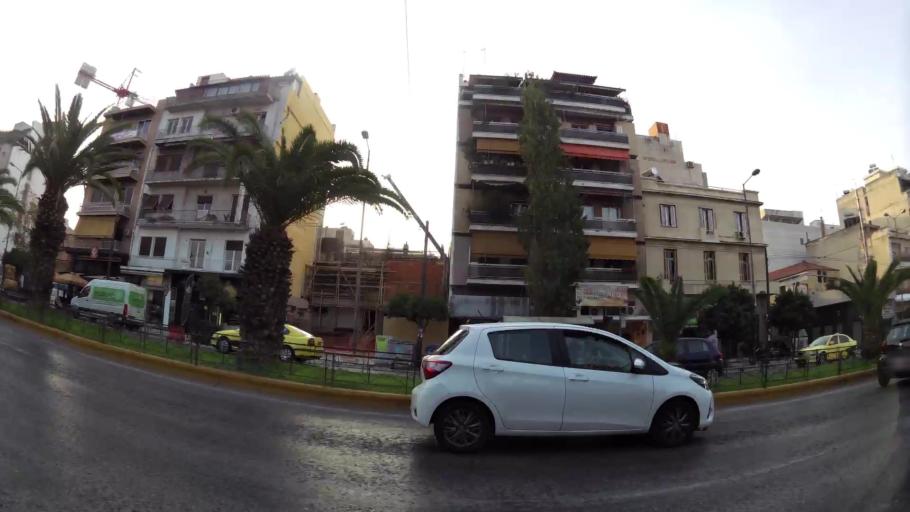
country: GR
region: Attica
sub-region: Nomarchia Athinas
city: Kallithea
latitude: 37.9602
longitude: 23.7081
